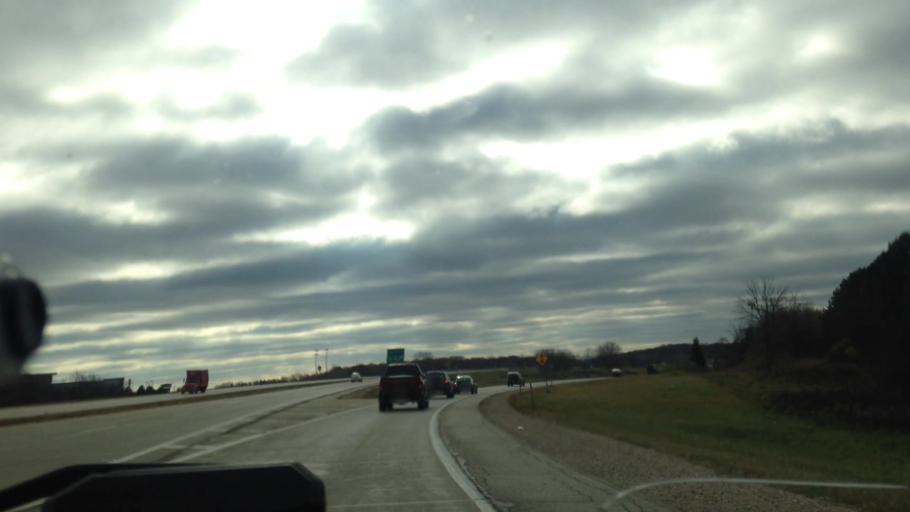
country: US
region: Wisconsin
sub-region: Washington County
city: West Bend
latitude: 43.4023
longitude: -88.1935
